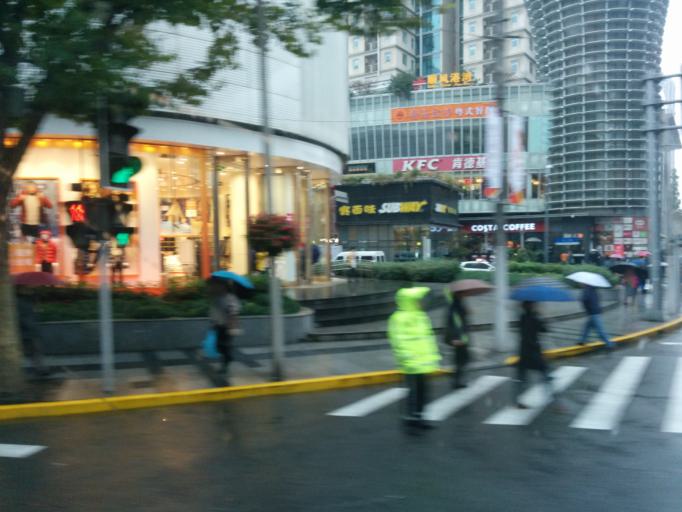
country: CN
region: Shanghai Shi
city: Shanghai
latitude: 31.2310
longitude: 121.4539
